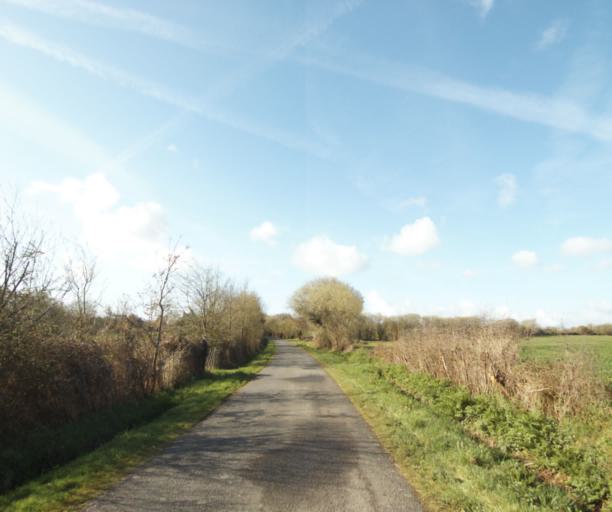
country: FR
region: Pays de la Loire
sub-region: Departement de la Loire-Atlantique
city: Bouvron
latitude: 47.4081
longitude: -1.8480
